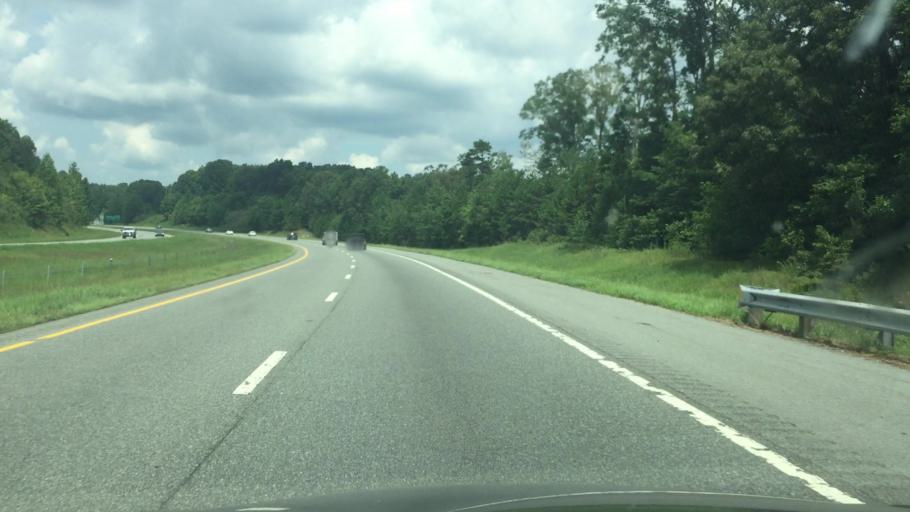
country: US
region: North Carolina
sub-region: Randolph County
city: Asheboro
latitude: 35.5844
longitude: -79.8072
